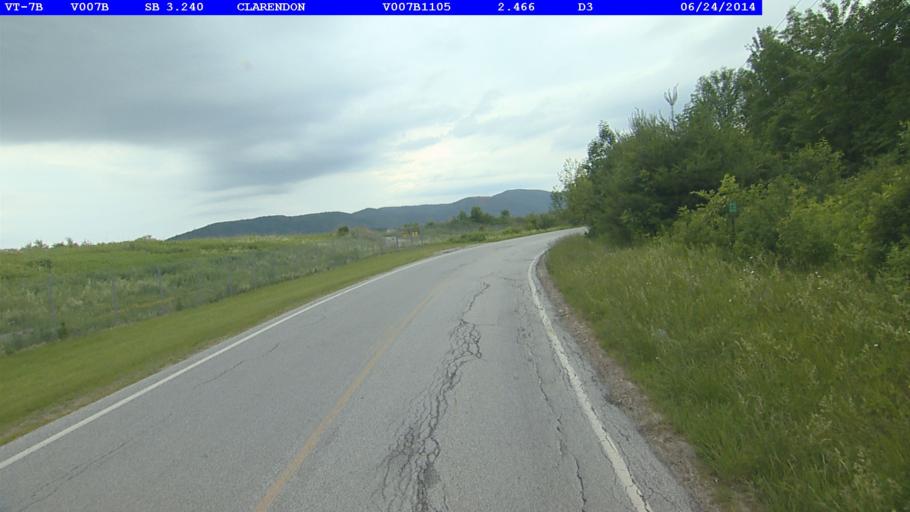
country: US
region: Vermont
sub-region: Rutland County
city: Rutland
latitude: 43.5347
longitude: -72.9521
